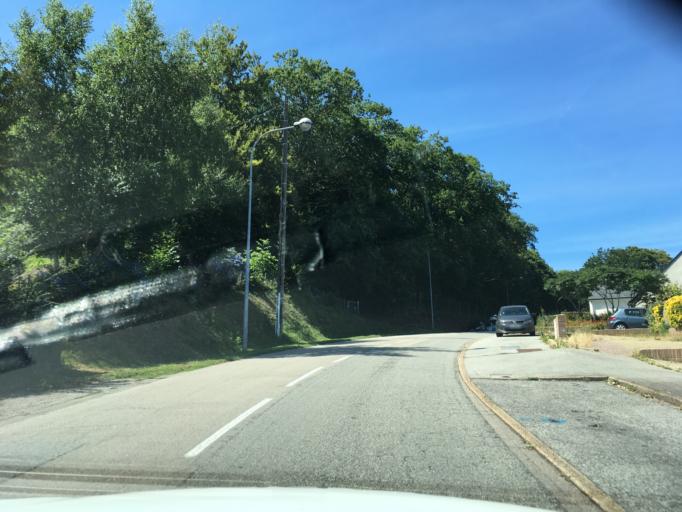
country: FR
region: Brittany
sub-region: Departement du Finistere
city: Quimper
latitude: 47.9815
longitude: -4.1301
